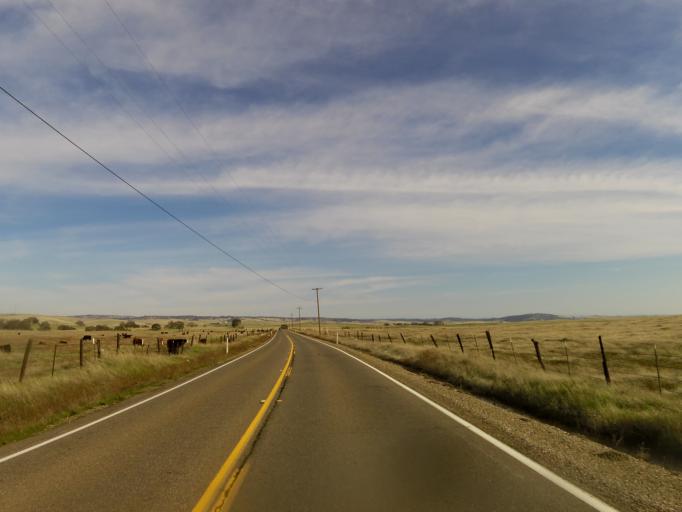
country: US
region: California
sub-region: Sacramento County
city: Folsom
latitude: 38.6182
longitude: -121.1316
